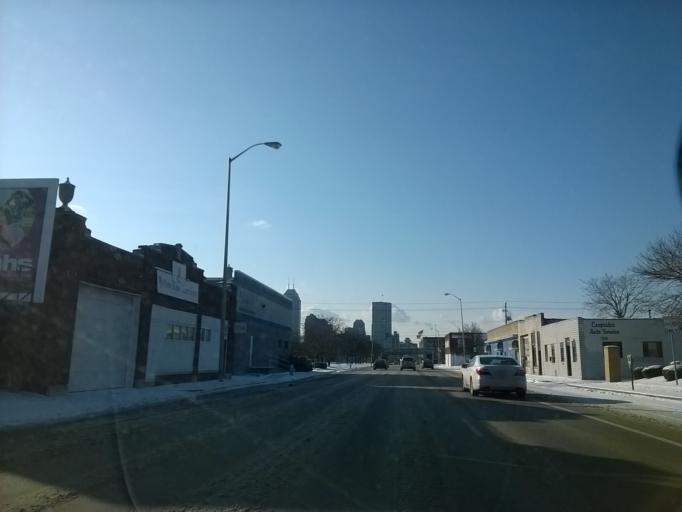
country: US
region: Indiana
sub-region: Marion County
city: Indianapolis
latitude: 39.7856
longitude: -86.1613
